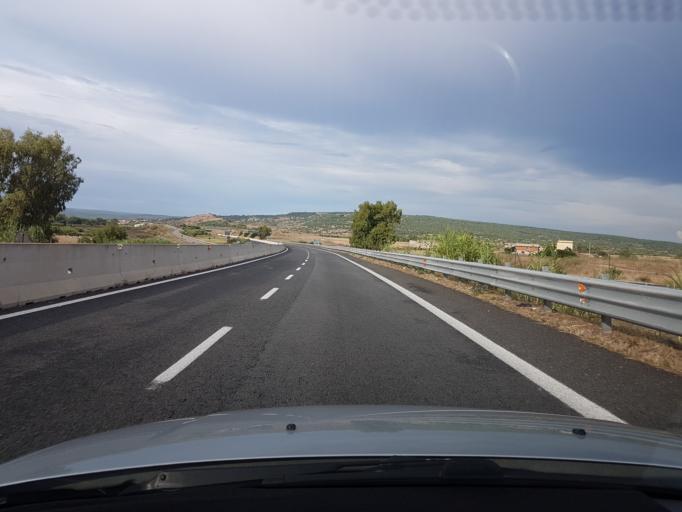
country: IT
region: Sardinia
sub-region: Provincia di Oristano
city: Tramatza
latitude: 39.9974
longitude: 8.6559
